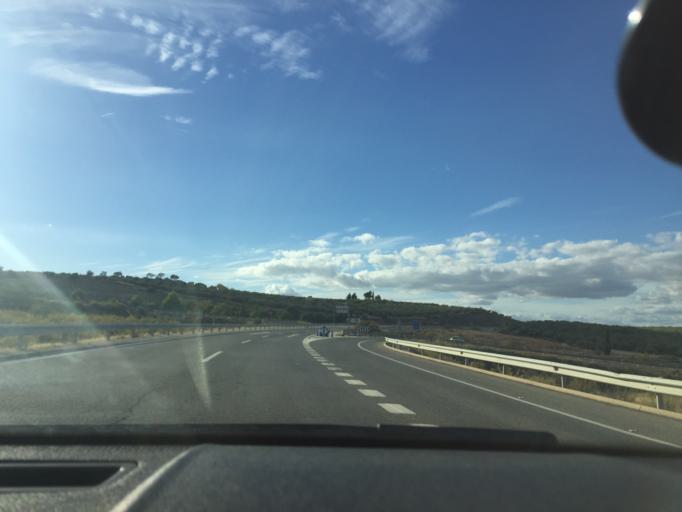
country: ES
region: Andalusia
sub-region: Provincia de Jaen
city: Torredonjimeno
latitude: 37.7524
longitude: -3.9555
